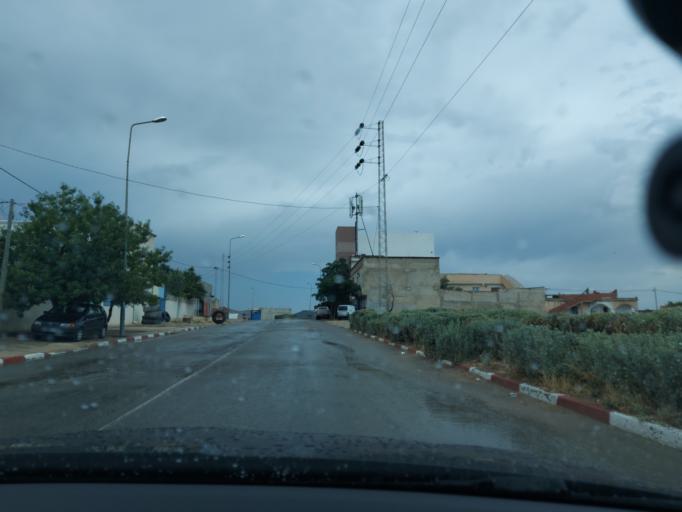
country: TN
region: Silyanah
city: Maktar
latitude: 35.8556
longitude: 9.2109
